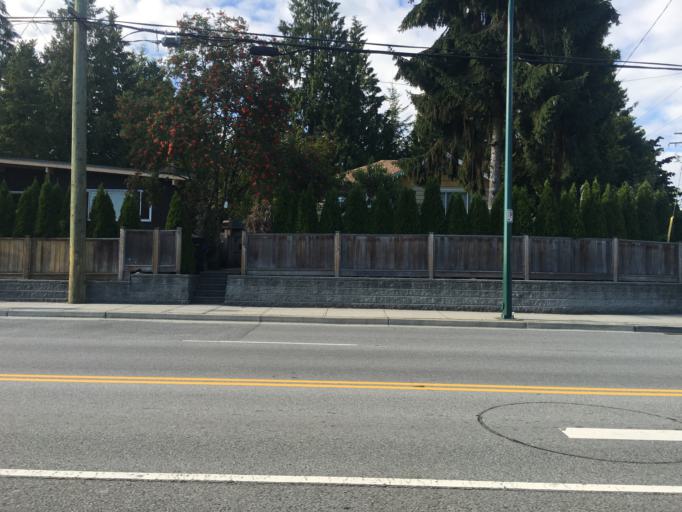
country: CA
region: British Columbia
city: Port Moody
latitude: 49.2489
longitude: -122.8471
